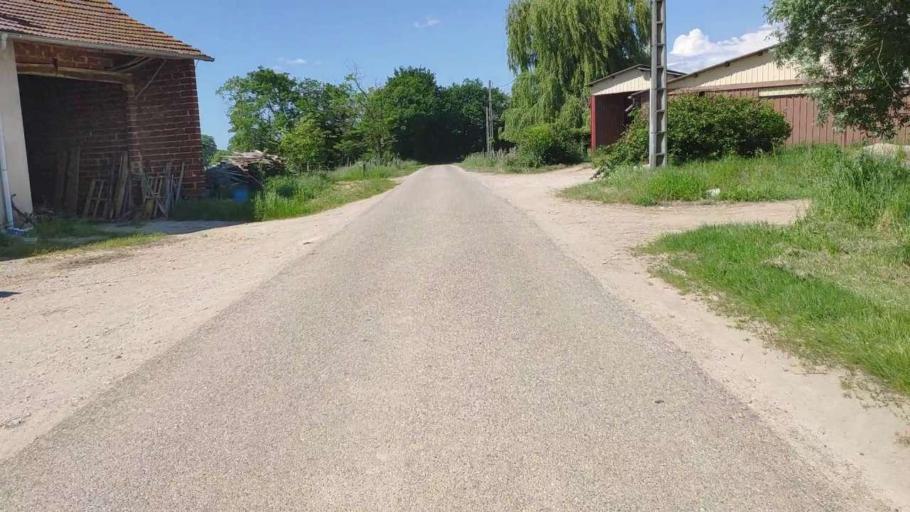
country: FR
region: Franche-Comte
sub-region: Departement du Jura
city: Bletterans
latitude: 46.7985
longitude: 5.4080
